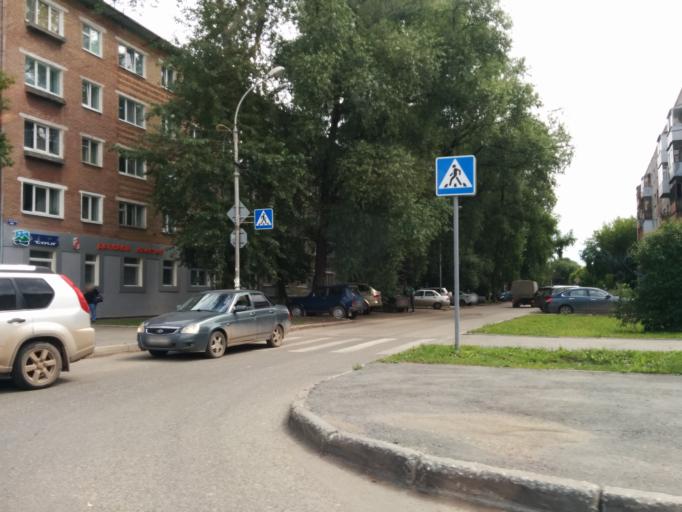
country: RU
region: Perm
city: Perm
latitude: 58.0037
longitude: 56.2516
